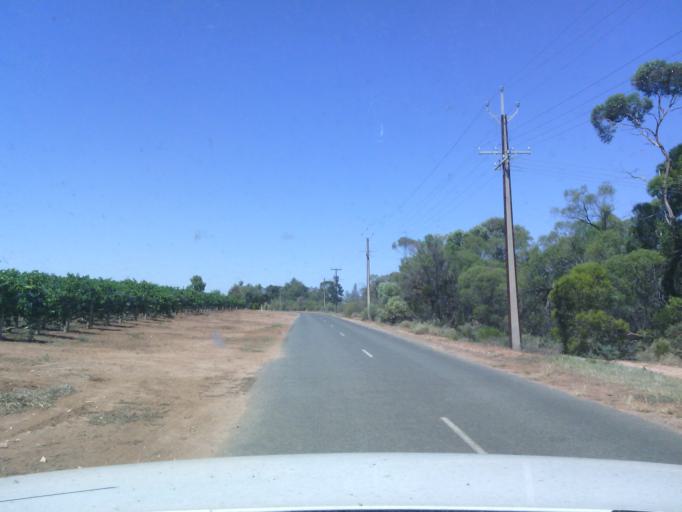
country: AU
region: South Australia
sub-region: Berri and Barmera
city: Berri
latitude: -34.2805
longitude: 140.5585
